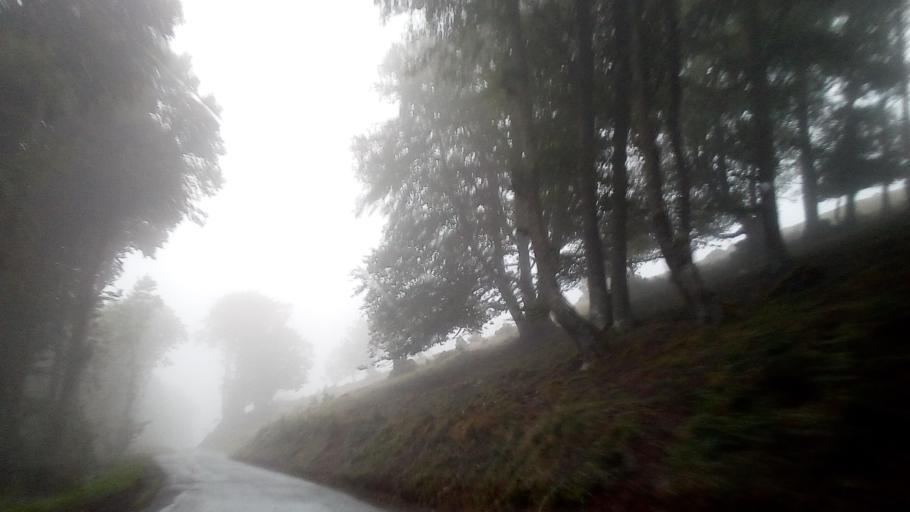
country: FR
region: Midi-Pyrenees
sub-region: Departement des Hautes-Pyrenees
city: Saint-Lary-Soulan
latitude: 42.9072
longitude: 0.2922
